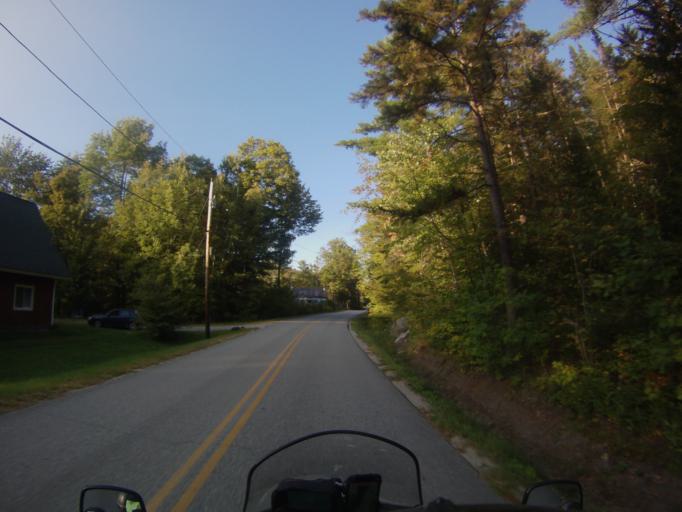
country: US
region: Vermont
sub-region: Addison County
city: Middlebury (village)
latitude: 43.9935
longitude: -73.0305
